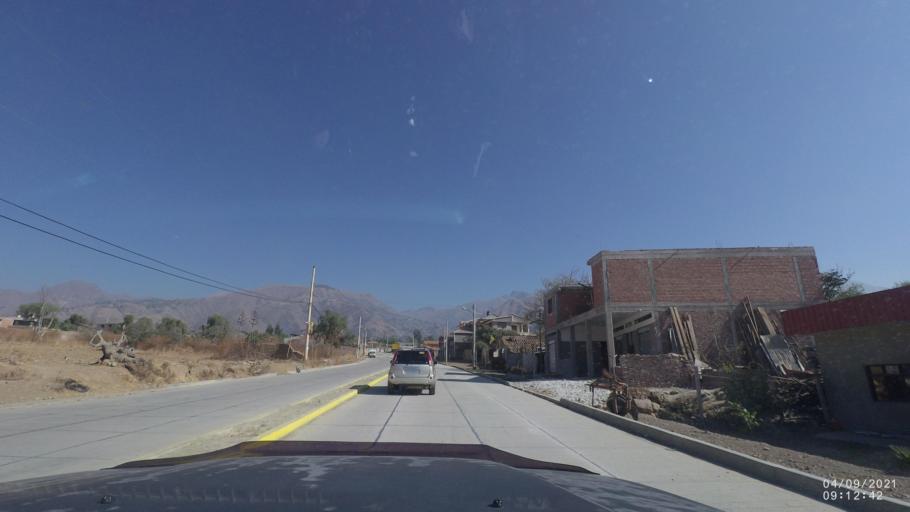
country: BO
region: Cochabamba
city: Sipe Sipe
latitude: -17.3844
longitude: -66.3397
